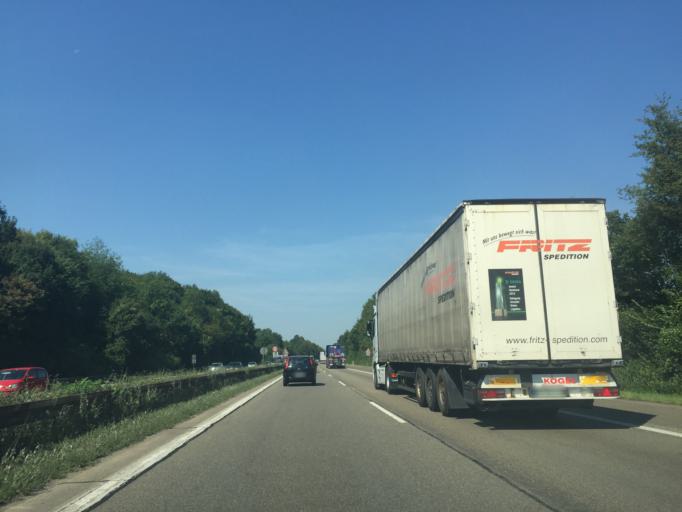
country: DE
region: Baden-Wuerttemberg
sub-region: Karlsruhe Region
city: Balzfeld
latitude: 49.2579
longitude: 8.8259
